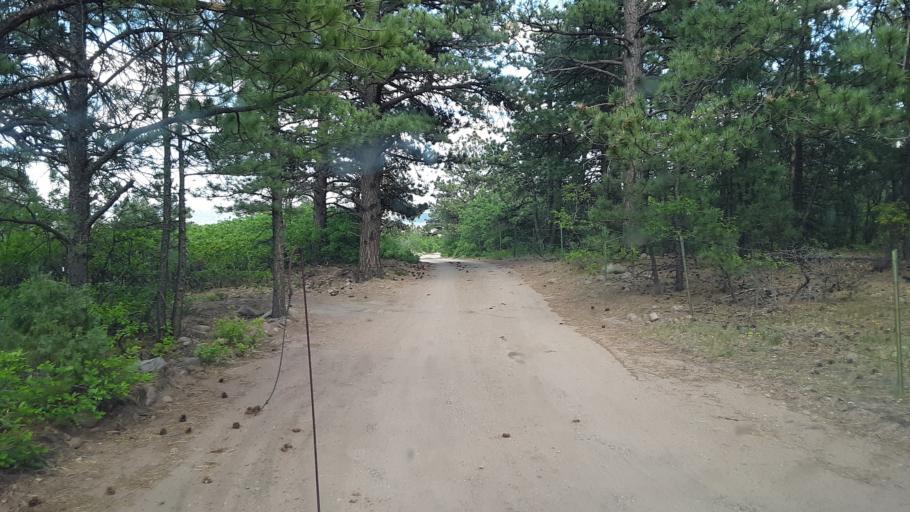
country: US
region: Colorado
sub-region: Custer County
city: Westcliffe
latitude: 38.2217
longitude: -105.6170
